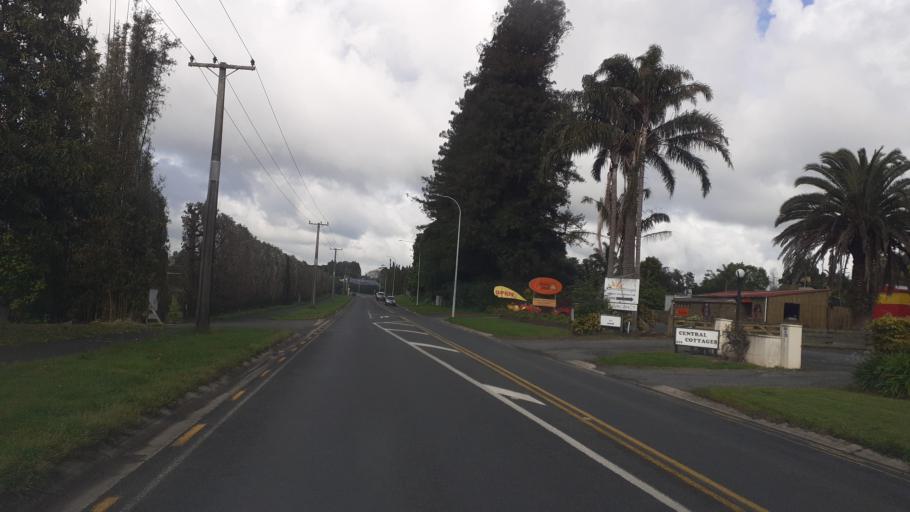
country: NZ
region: Northland
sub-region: Far North District
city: Kerikeri
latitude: -35.2383
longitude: 173.9397
